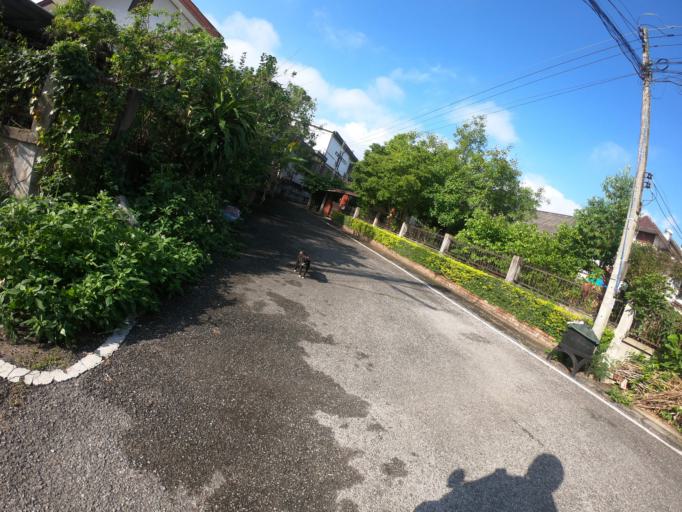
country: TH
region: Chiang Mai
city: Chiang Mai
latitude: 18.8129
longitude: 98.9667
